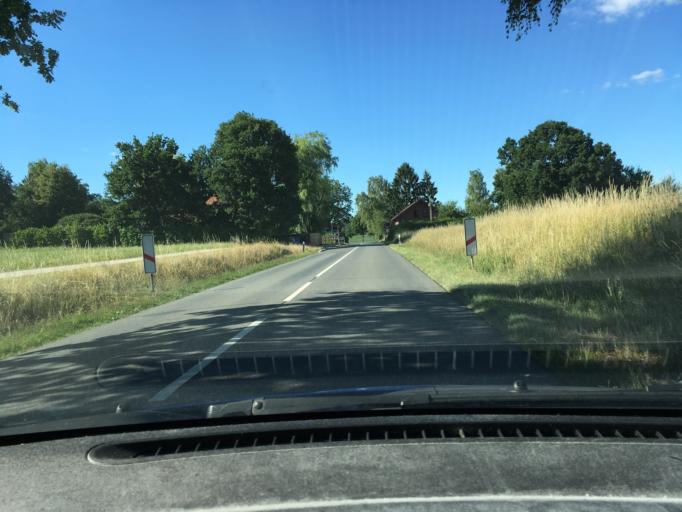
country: DE
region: Lower Saxony
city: Thomasburg
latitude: 53.1865
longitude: 10.6298
